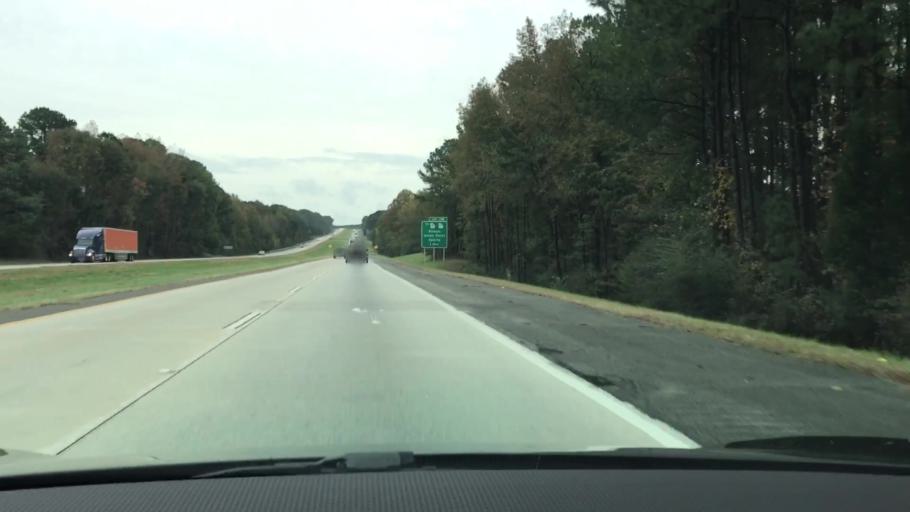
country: US
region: Georgia
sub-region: Greene County
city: Union Point
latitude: 33.5466
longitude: -83.1046
